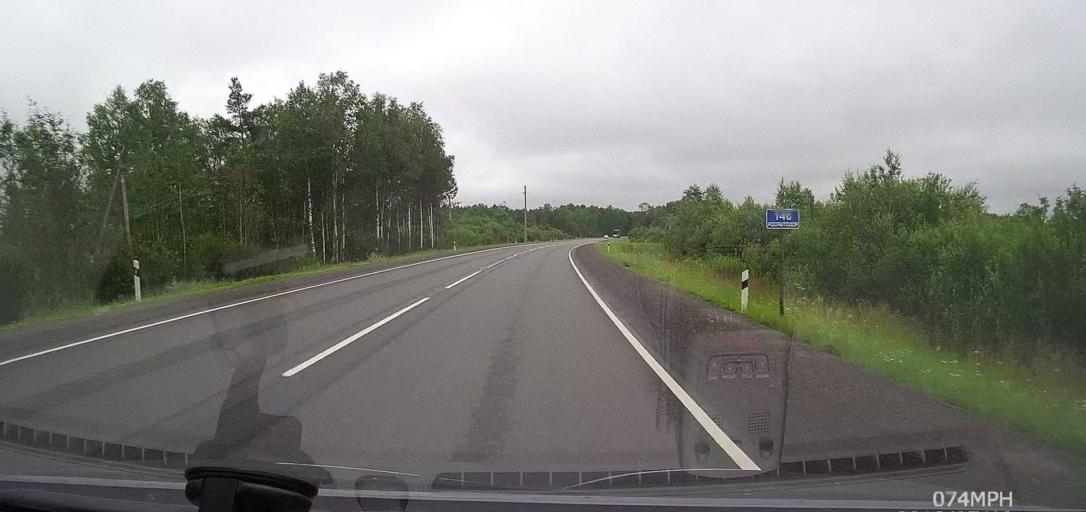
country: RU
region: Leningrad
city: Syas'stroy
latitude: 60.2059
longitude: 32.6801
